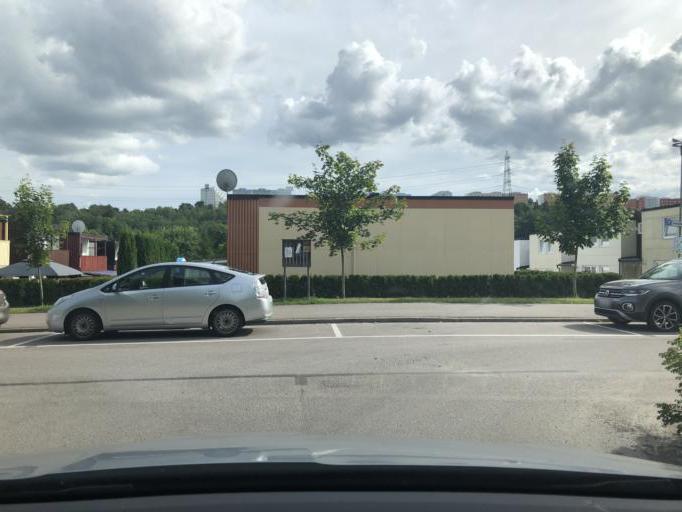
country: SE
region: Stockholm
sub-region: Botkyrka Kommun
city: Fittja
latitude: 59.2472
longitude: 17.8512
